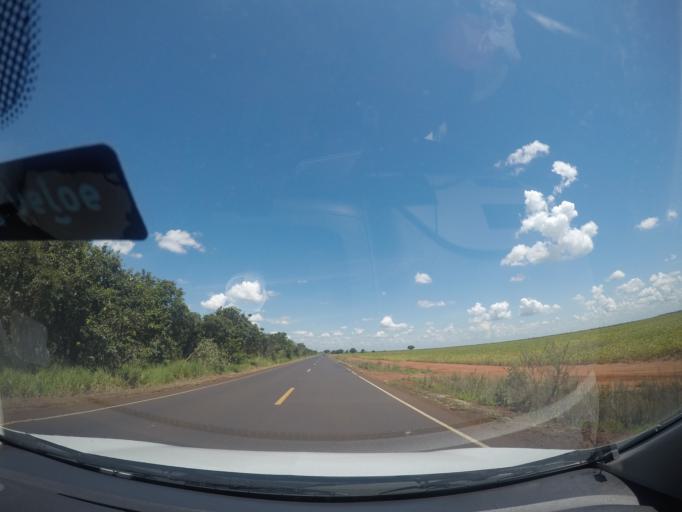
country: BR
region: Minas Gerais
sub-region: Frutal
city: Frutal
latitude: -19.7103
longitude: -48.7696
